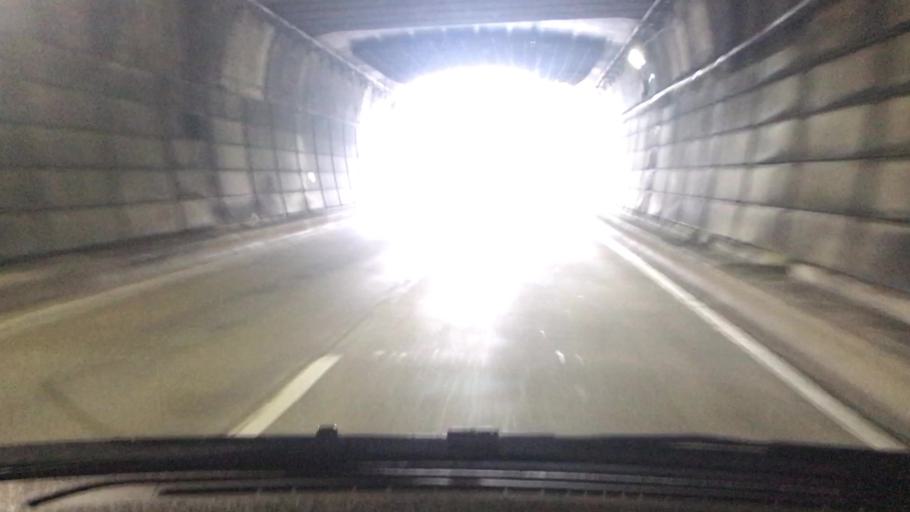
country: JP
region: Hyogo
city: Kobe
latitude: 34.7627
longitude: 135.1544
